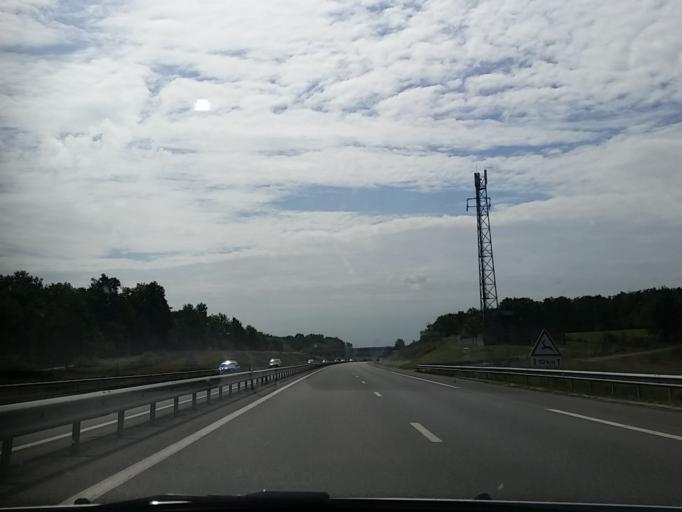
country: FR
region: Auvergne
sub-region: Departement de l'Allier
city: Vallon-en-Sully
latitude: 46.5662
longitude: 2.5403
